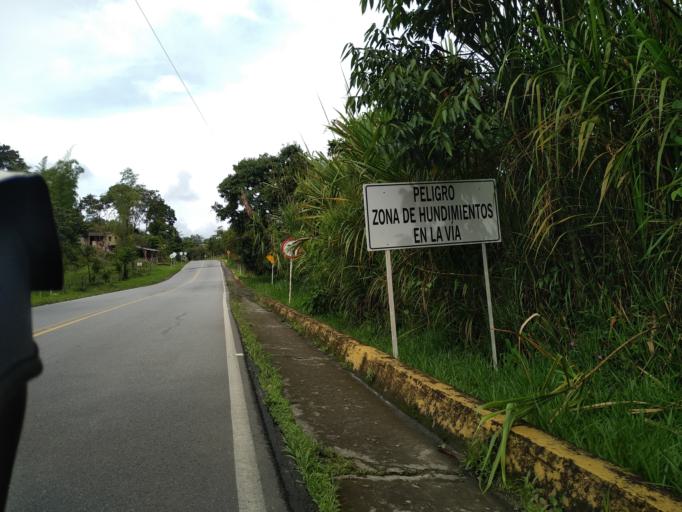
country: CO
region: Santander
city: Suaita
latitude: 6.0956
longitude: -73.3831
